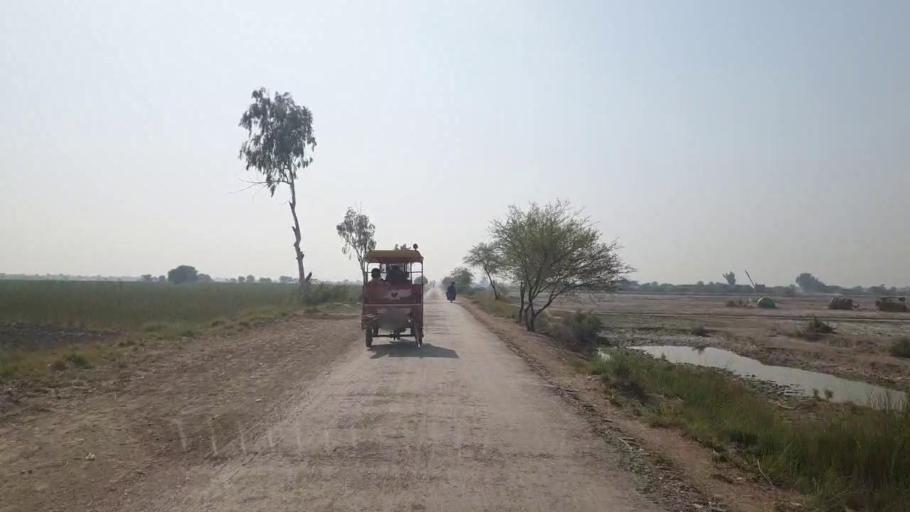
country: PK
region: Sindh
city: Shahdadpur
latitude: 25.9233
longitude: 68.7351
